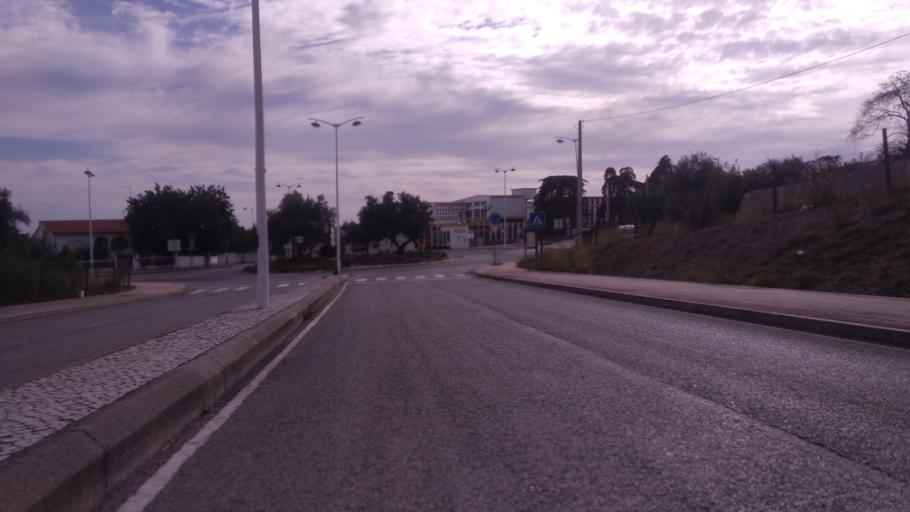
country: PT
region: Faro
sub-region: Sao Bras de Alportel
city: Sao Bras de Alportel
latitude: 37.1540
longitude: -7.8978
